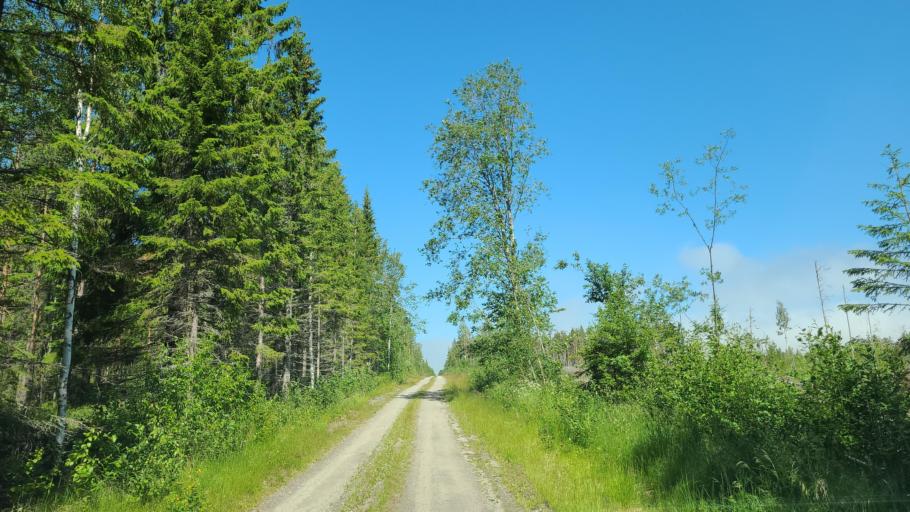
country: SE
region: Vaesternorrland
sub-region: OErnskoeldsviks Kommun
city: Husum
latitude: 63.4307
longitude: 19.2285
